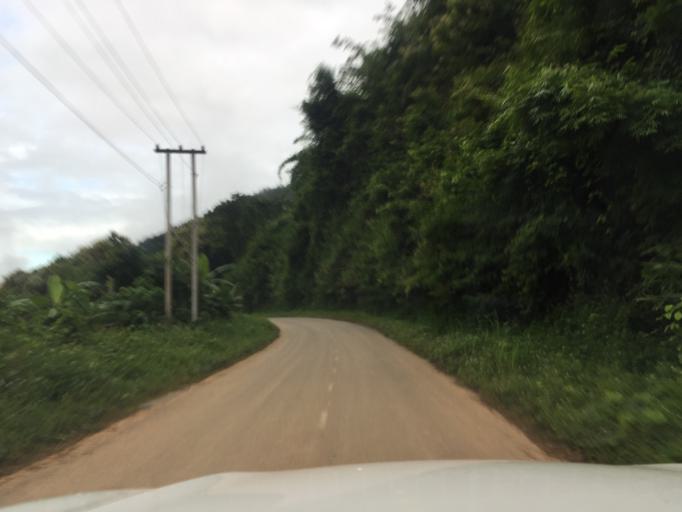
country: LA
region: Phongsali
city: Khoa
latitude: 21.0796
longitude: 102.3743
